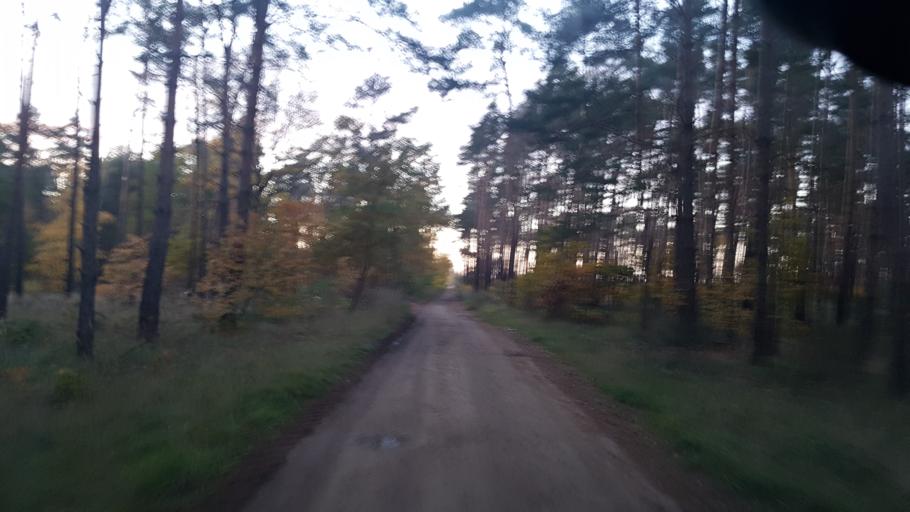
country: DE
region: Brandenburg
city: Bad Liebenwerda
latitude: 51.5078
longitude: 13.3194
